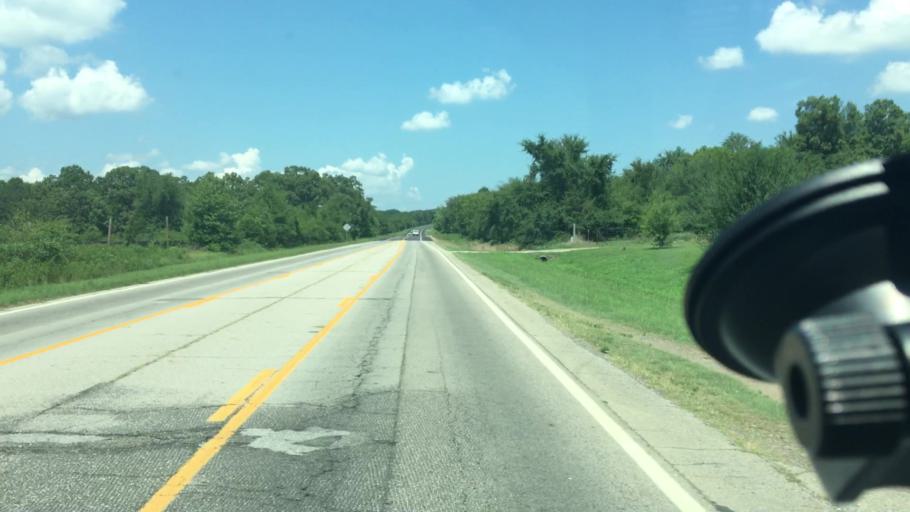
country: US
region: Arkansas
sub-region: Sebastian County
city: Lavaca
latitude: 35.2968
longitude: -94.1488
